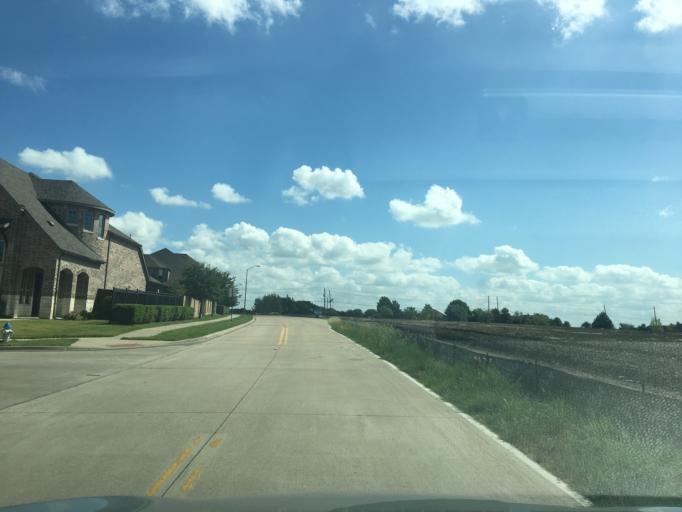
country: US
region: Texas
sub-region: Dallas County
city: Sachse
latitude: 32.9573
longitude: -96.5728
